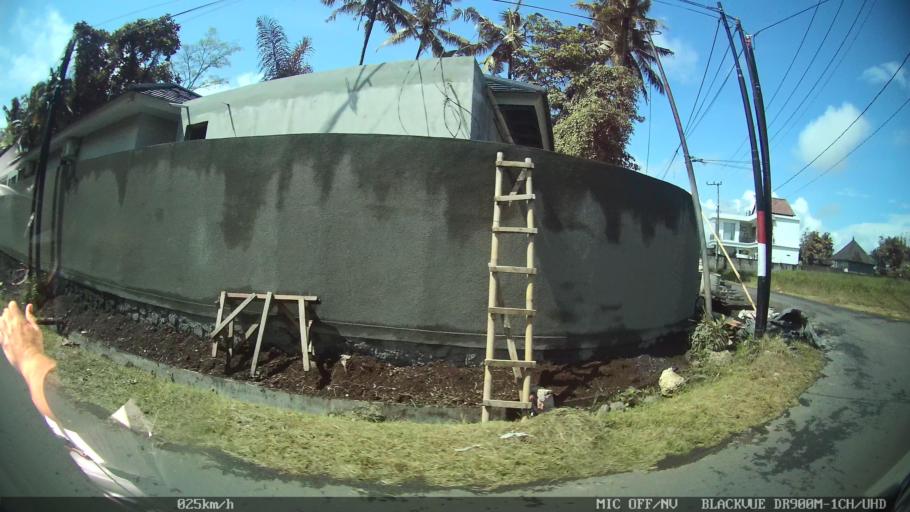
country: ID
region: Bali
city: Banjar Tebongkang
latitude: -8.5442
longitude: 115.2686
